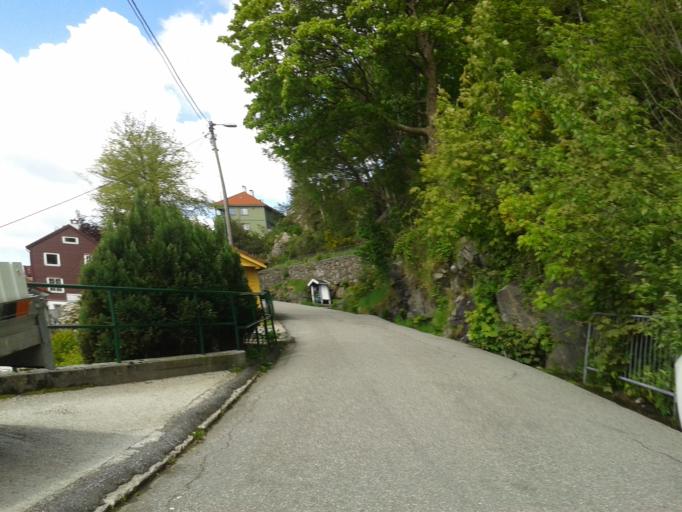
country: NO
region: Hordaland
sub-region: Bergen
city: Bergen
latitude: 60.4163
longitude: 5.3181
